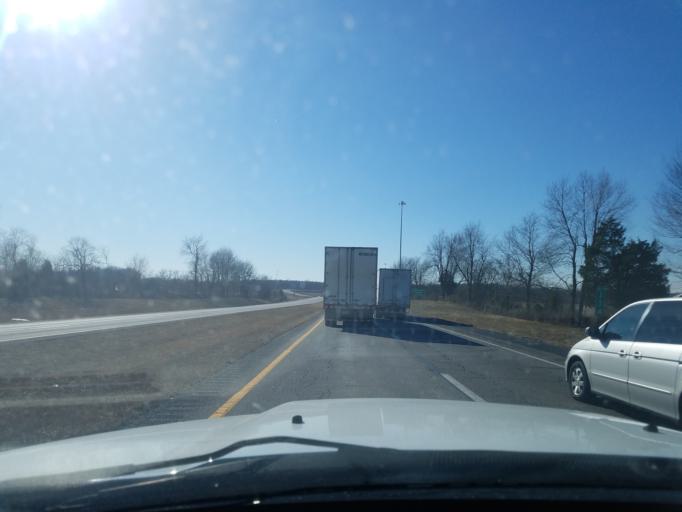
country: US
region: Kentucky
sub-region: Hardin County
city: Elizabethtown
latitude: 37.6593
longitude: -85.8855
